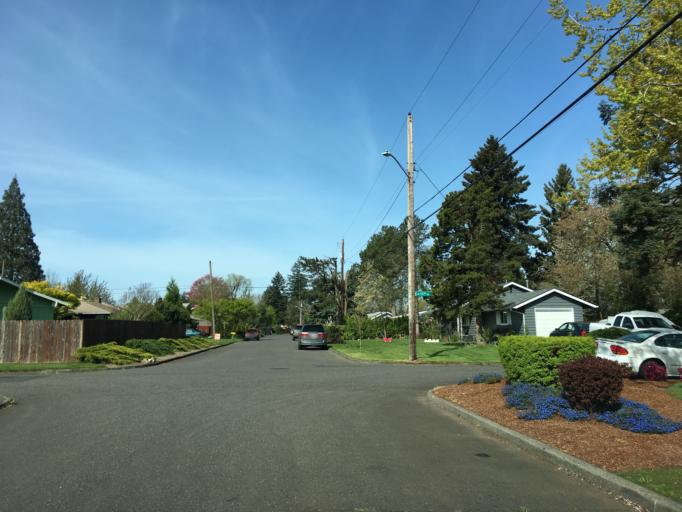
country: US
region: Oregon
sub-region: Multnomah County
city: Lents
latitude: 45.5354
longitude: -122.5313
